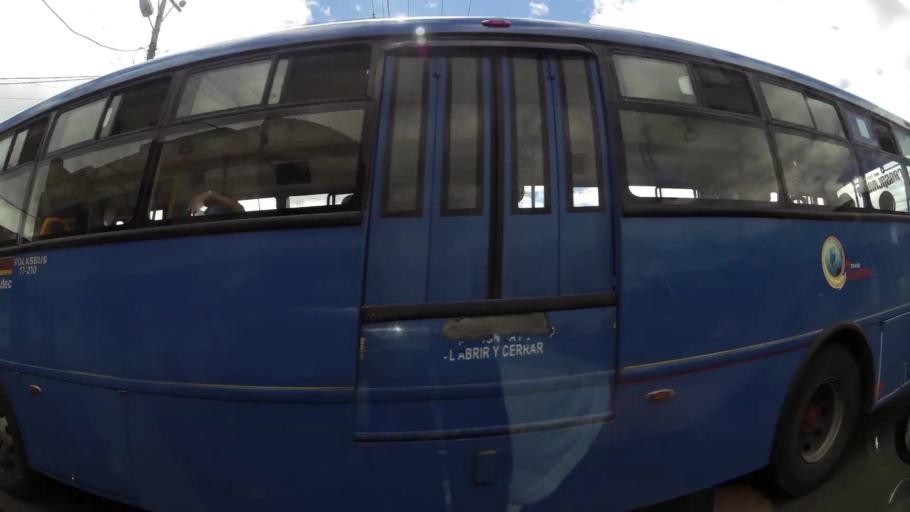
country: EC
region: Pichincha
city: Sangolqui
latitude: -0.3423
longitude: -78.5669
